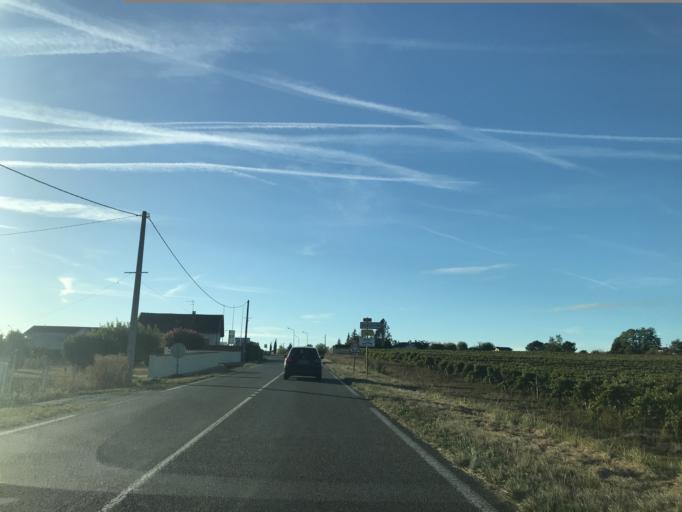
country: FR
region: Poitou-Charentes
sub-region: Departement de la Charente-Maritime
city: Montguyon
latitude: 45.2116
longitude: -0.1736
